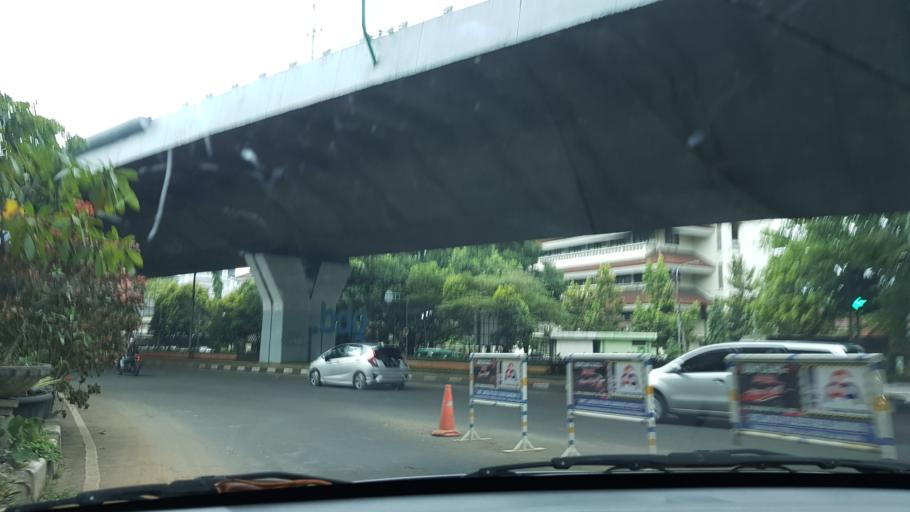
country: ID
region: West Java
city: Bandung
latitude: -6.8980
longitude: 107.6097
